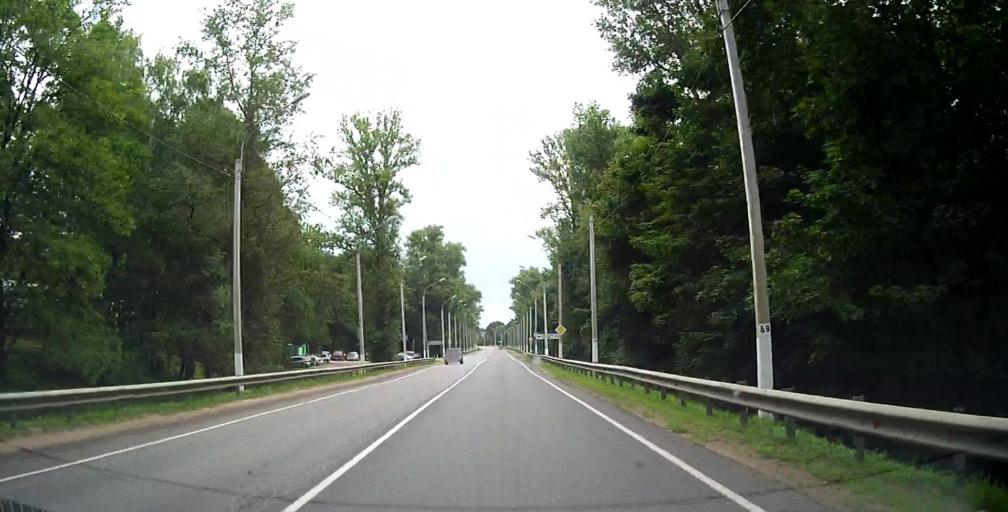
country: RU
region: Smolensk
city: Katyn'
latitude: 54.7660
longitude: 31.7335
